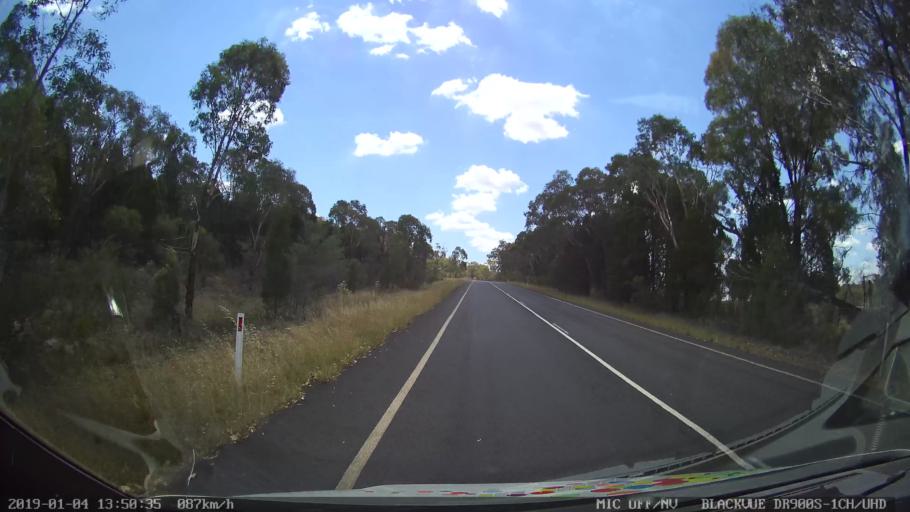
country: AU
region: New South Wales
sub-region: Dubbo Municipality
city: Dubbo
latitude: -32.4179
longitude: 148.5719
